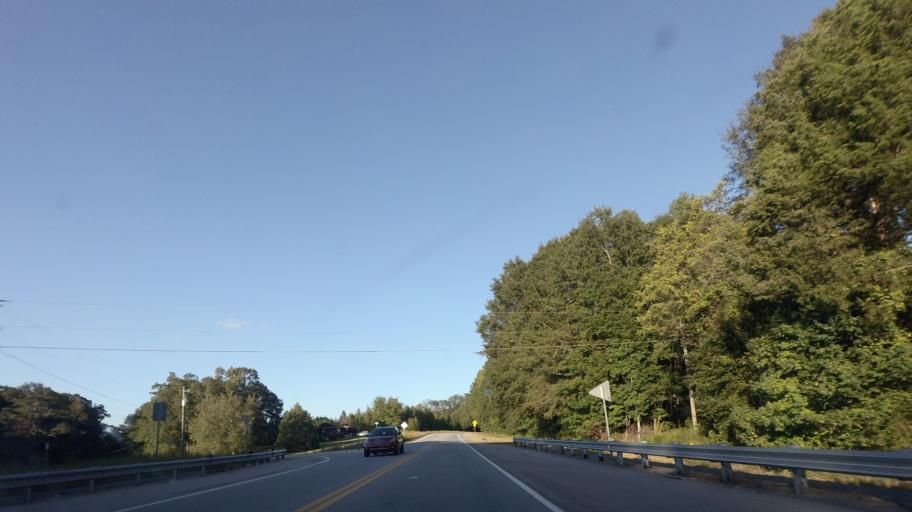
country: US
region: Georgia
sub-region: Spalding County
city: East Griffin
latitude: 33.2655
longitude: -84.2174
